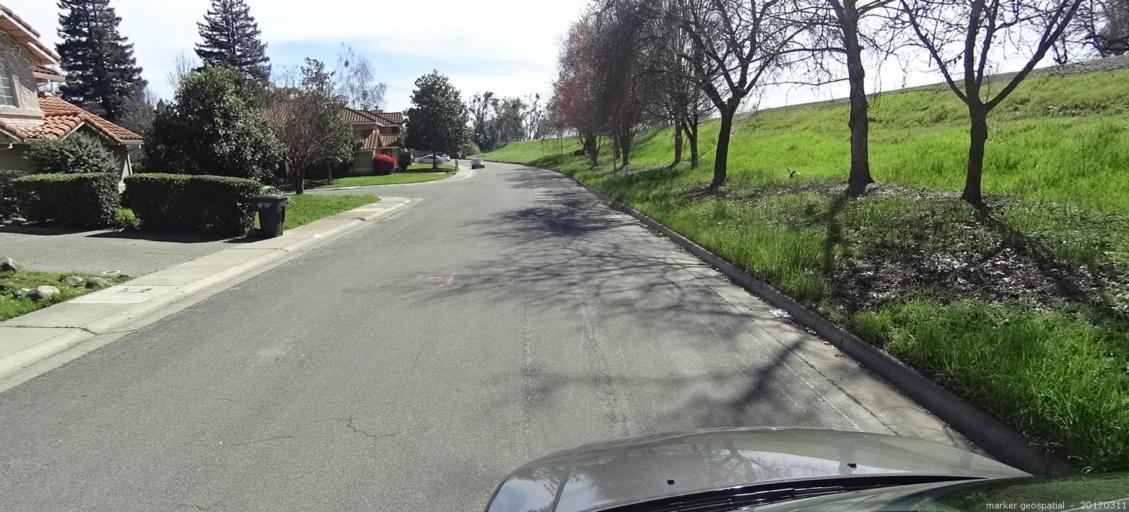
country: US
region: California
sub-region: Sacramento County
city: Parkway
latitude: 38.4808
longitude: -121.5449
